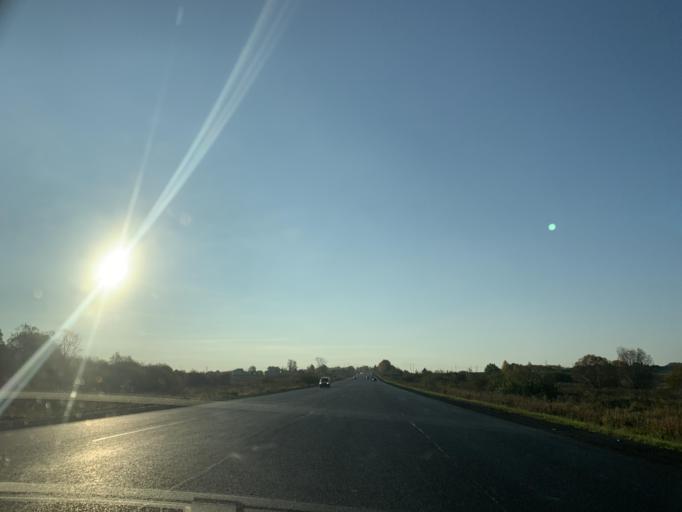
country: RU
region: Jaroslavl
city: Konstantinovskiy
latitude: 57.7950
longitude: 39.6020
